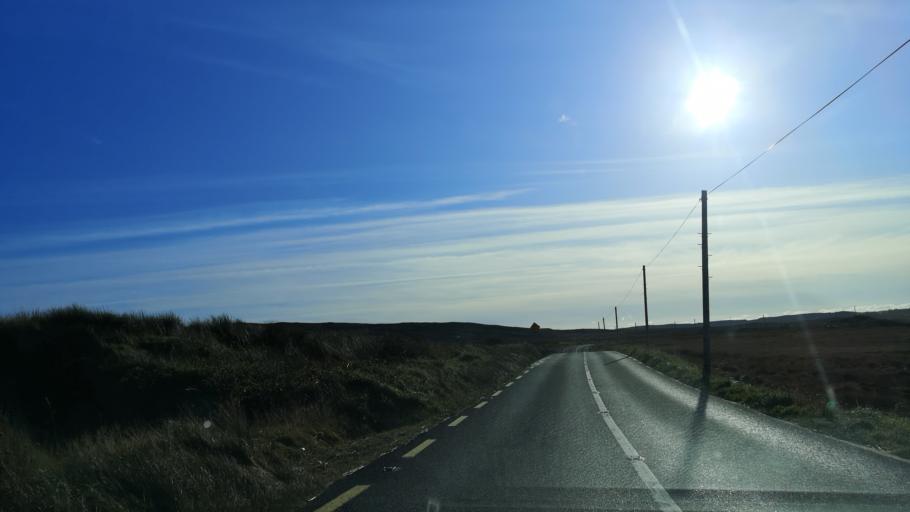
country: IE
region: Connaught
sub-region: County Galway
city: Clifden
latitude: 53.5392
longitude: -10.0300
